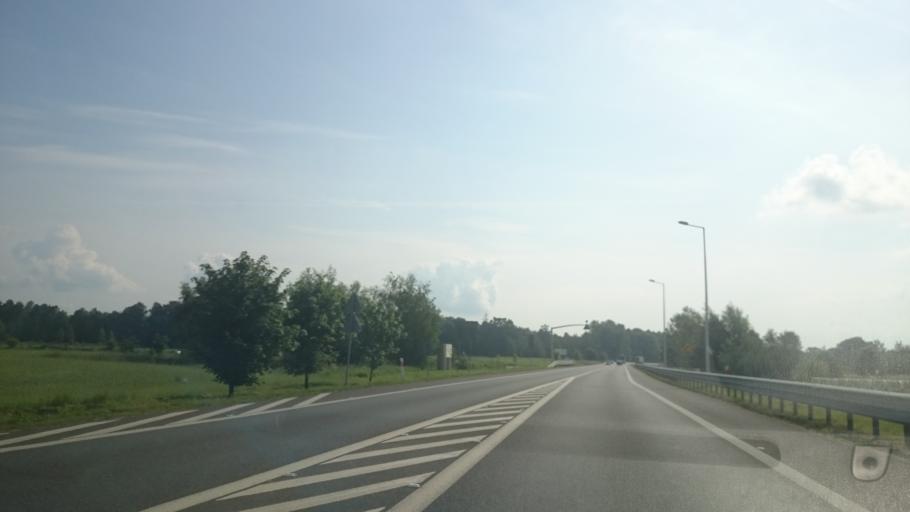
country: PL
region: Opole Voivodeship
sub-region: Powiat opolski
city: Chrzastowice
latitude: 50.6694
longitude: 18.0755
